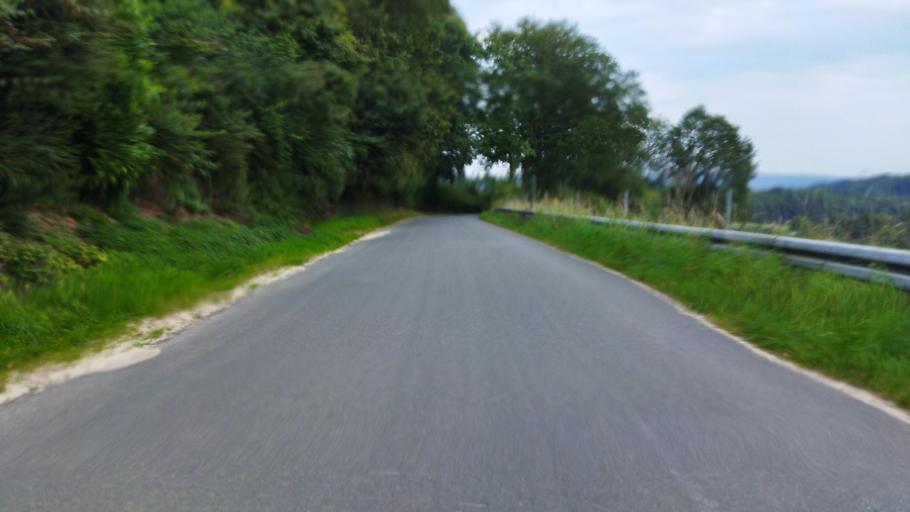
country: DE
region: Lower Saxony
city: Bad Iburg
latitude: 52.1694
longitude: 8.0217
